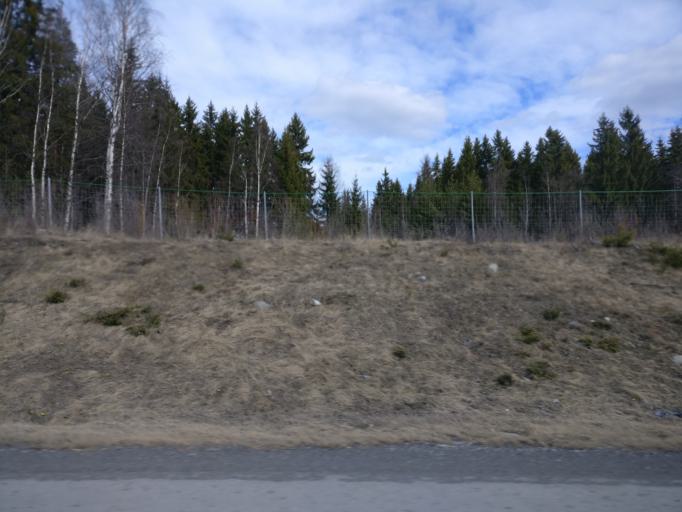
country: FI
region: Pirkanmaa
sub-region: Tampere
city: Lempaeaelae
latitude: 61.3252
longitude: 23.8077
